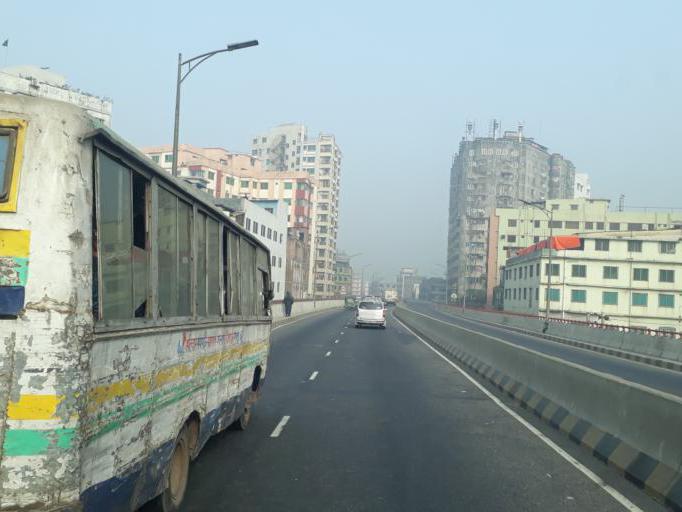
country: BD
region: Dhaka
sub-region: Dhaka
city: Dhaka
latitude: 23.7176
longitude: 90.4199
